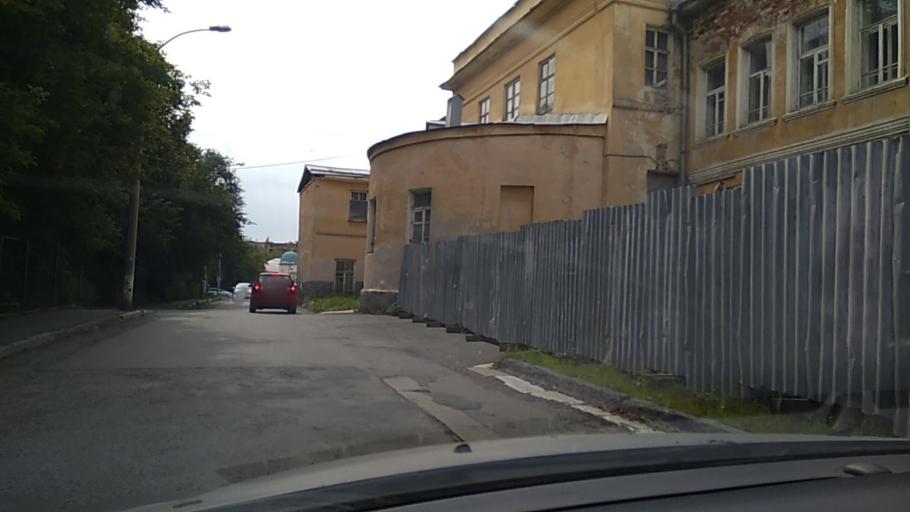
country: RU
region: Sverdlovsk
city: Yekaterinburg
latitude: 56.8221
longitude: 60.6010
